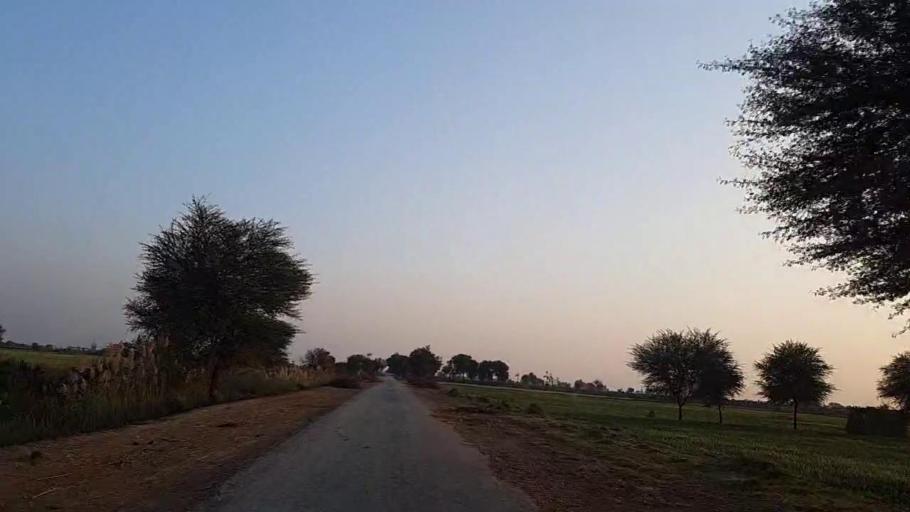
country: PK
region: Sindh
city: Shahdadpur
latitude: 25.9386
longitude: 68.5039
